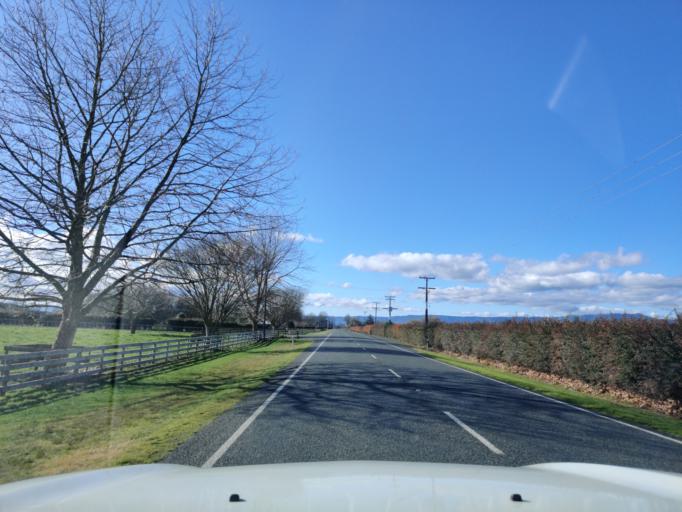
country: NZ
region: Waikato
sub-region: Matamata-Piako District
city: Matamata
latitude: -37.8715
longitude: 175.7453
